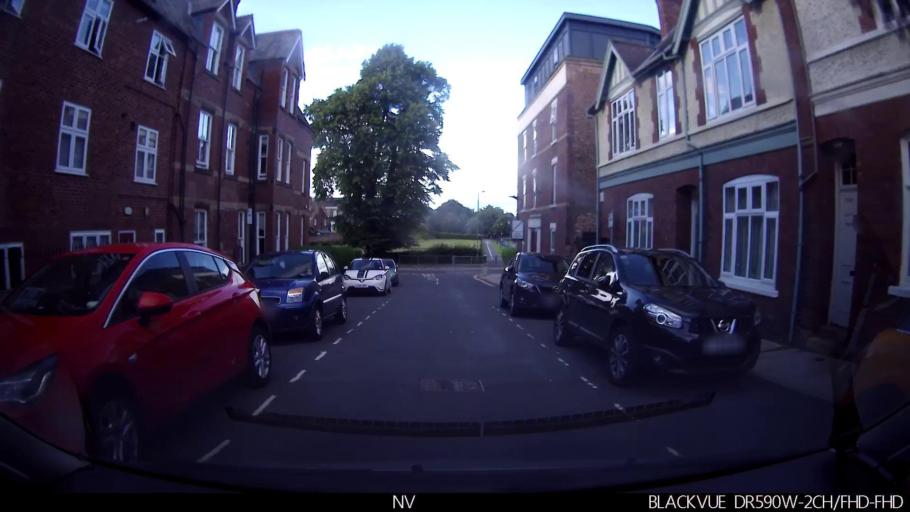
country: GB
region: England
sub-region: City of York
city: York
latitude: 53.9514
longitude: -1.0927
